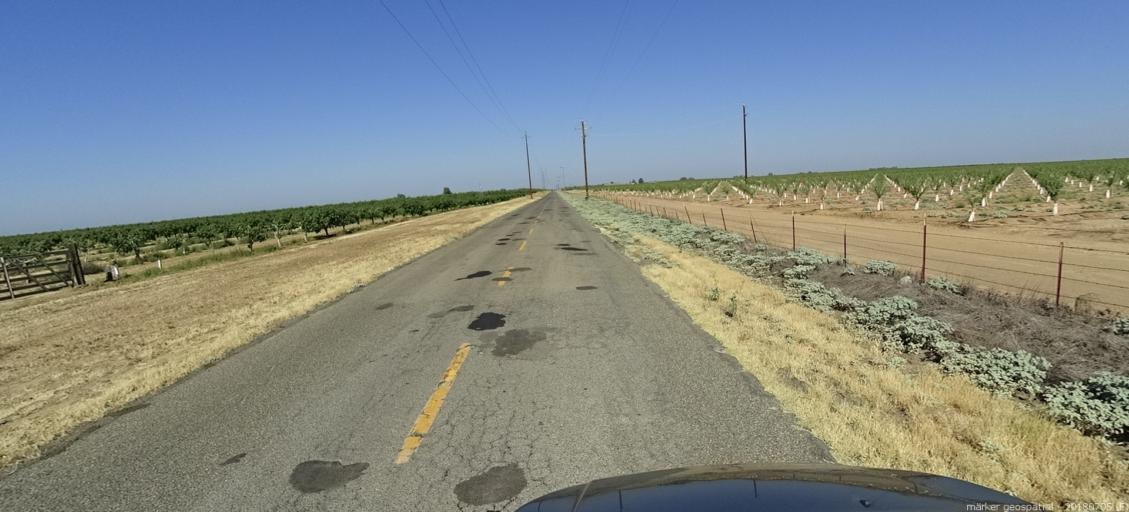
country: US
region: California
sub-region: Madera County
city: Fairmead
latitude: 37.1269
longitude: -120.0972
